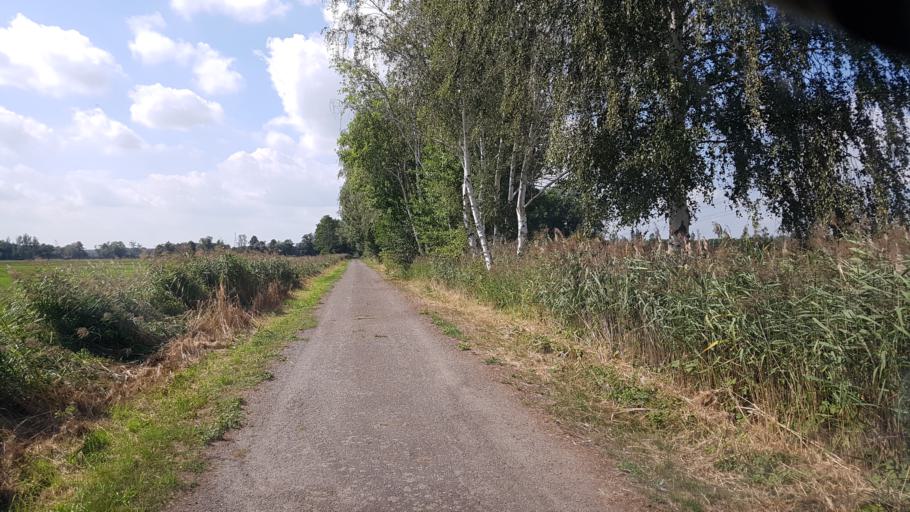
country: DE
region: Brandenburg
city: Lubbenau
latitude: 51.8929
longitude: 13.9308
